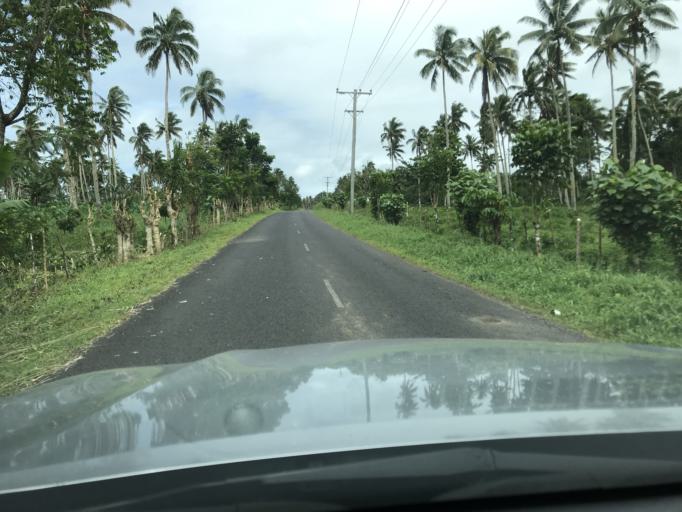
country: WS
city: Nofoali`i
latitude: -13.8730
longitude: -171.9211
